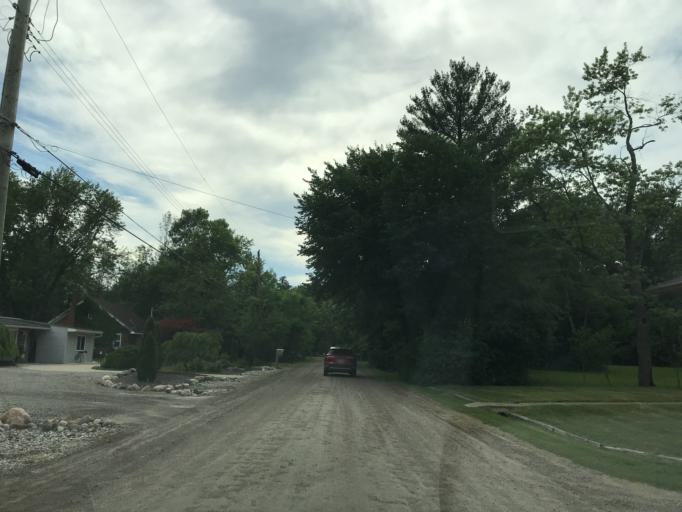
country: US
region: Michigan
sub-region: Oakland County
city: Farmington
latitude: 42.4458
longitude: -83.3385
